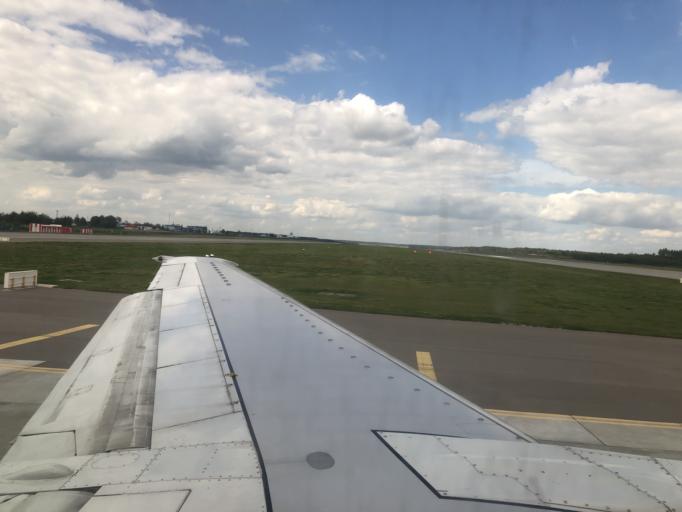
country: BY
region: Minsk
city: Smilavichy
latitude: 53.8795
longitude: 28.0680
